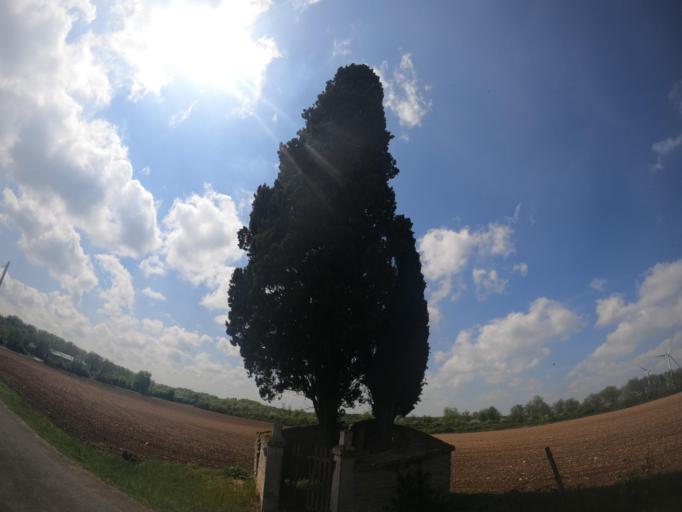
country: FR
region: Poitou-Charentes
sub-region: Departement des Deux-Sevres
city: Saint-Varent
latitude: 46.8567
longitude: -0.2069
